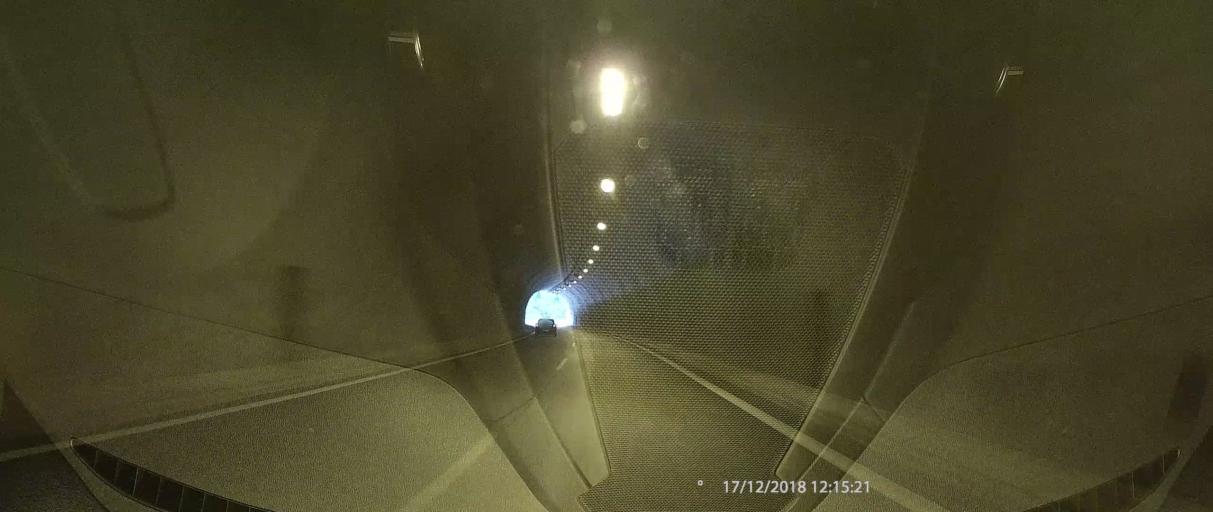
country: GR
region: Epirus
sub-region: Nomos Ioanninon
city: Katsikas
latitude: 39.7163
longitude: 21.0190
